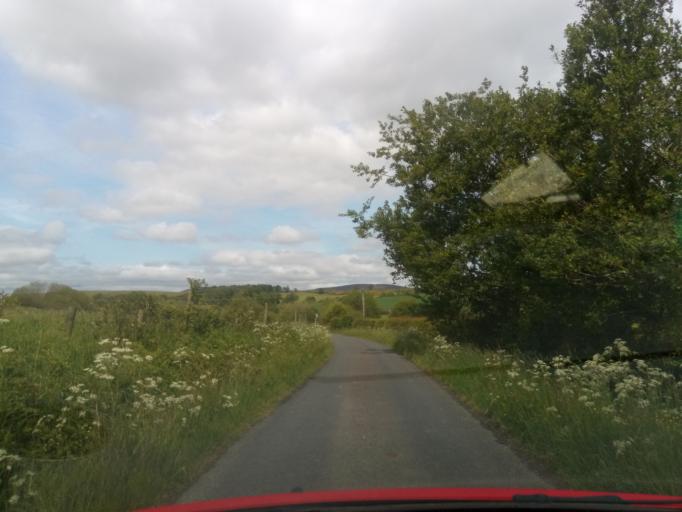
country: GB
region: Scotland
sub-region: The Scottish Borders
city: Selkirk
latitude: 55.5305
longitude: -2.8420
